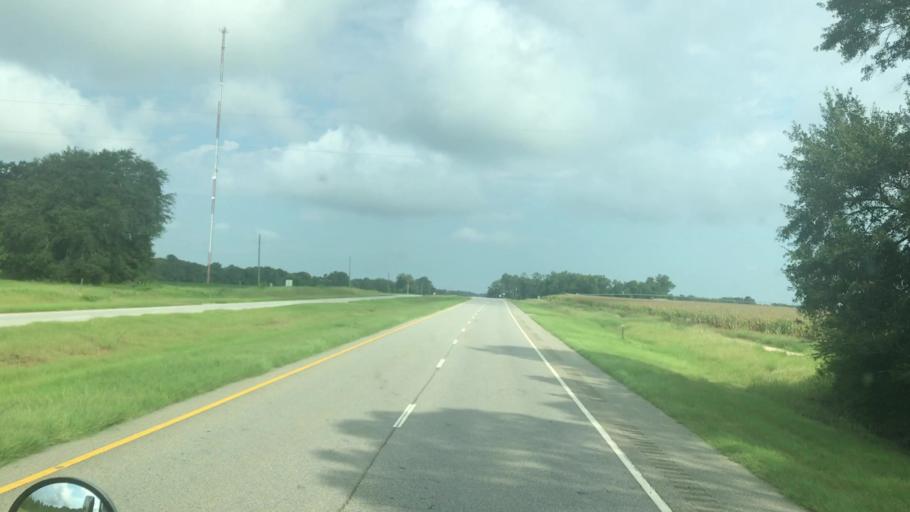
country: US
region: Georgia
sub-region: Miller County
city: Colquitt
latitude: 31.2624
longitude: -84.8147
